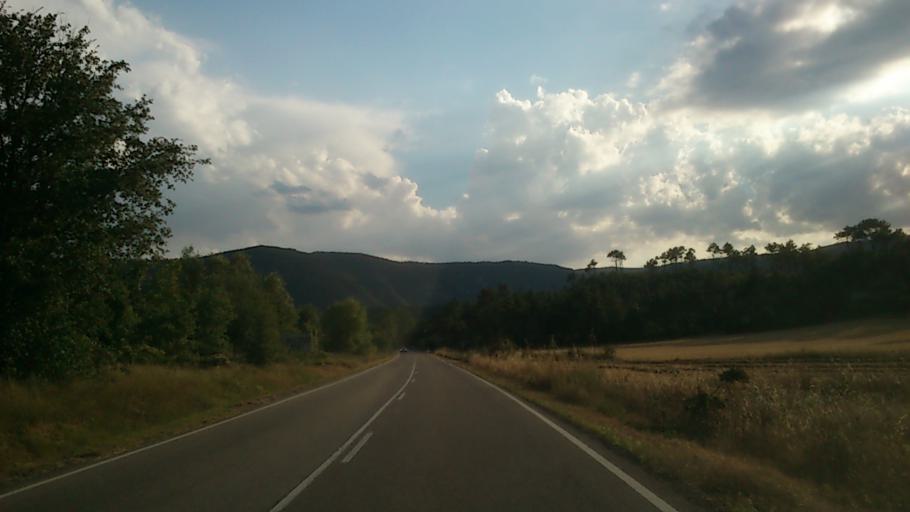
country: ES
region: Castille and Leon
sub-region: Provincia de Burgos
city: Trespaderne
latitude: 42.7922
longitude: -3.3476
